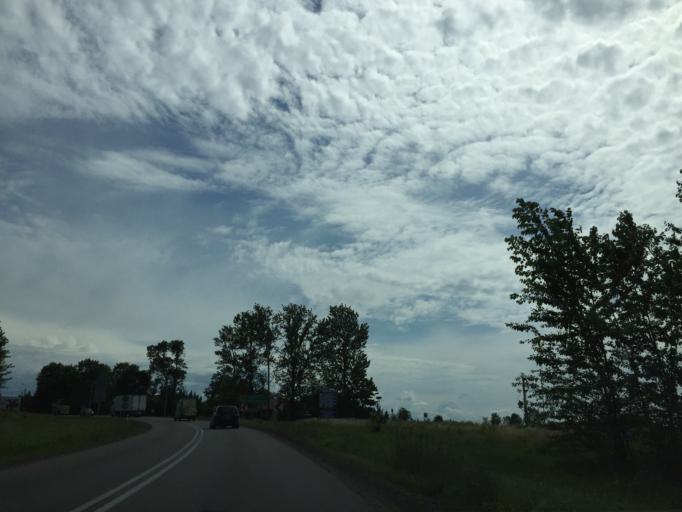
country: PL
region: Podlasie
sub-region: Powiat siemiatycki
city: Siemiatycze
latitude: 52.4425
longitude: 22.8506
